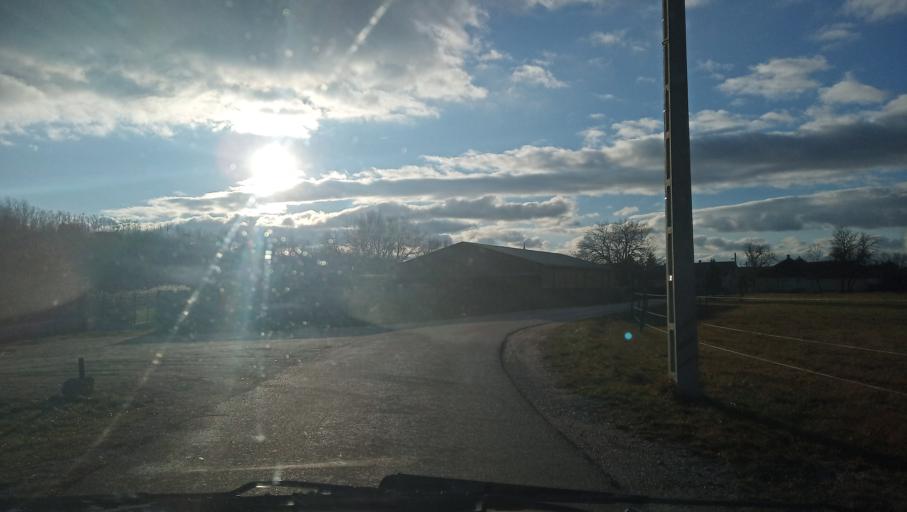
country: HU
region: Komarom-Esztergom
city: Piliscsev
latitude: 47.6811
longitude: 18.8243
